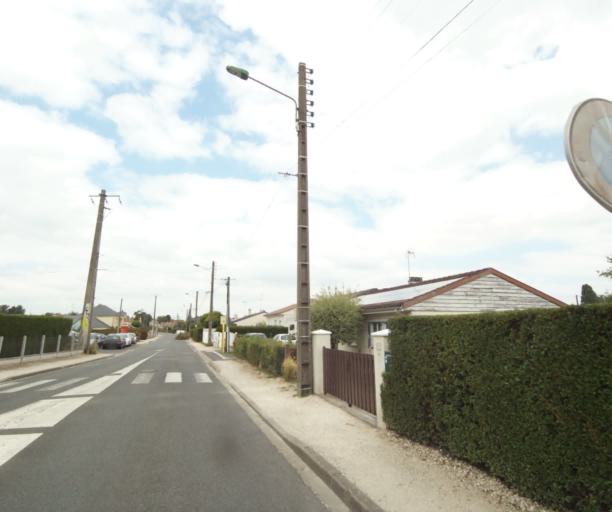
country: FR
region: Centre
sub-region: Departement du Loiret
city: Boigny-sur-Bionne
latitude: 47.9279
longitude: 2.0096
